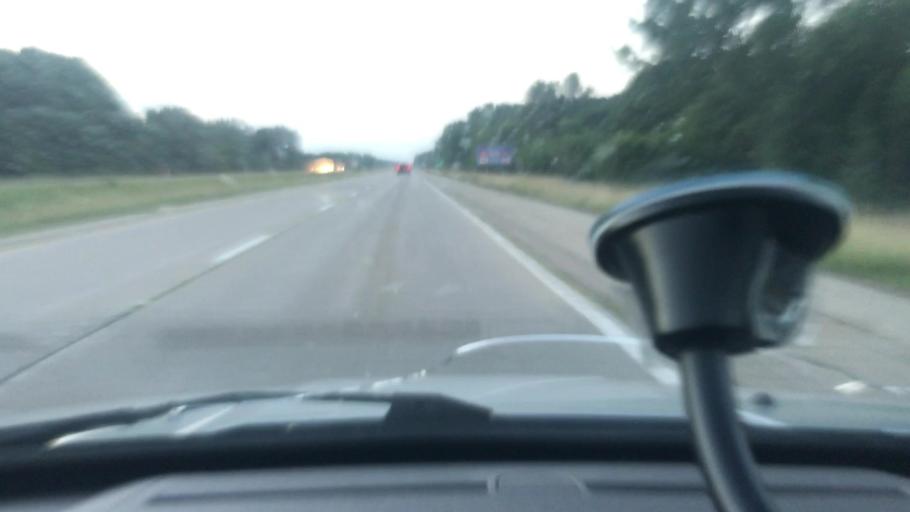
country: US
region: Illinois
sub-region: Peoria County
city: Bellevue
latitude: 40.7562
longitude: -89.6708
